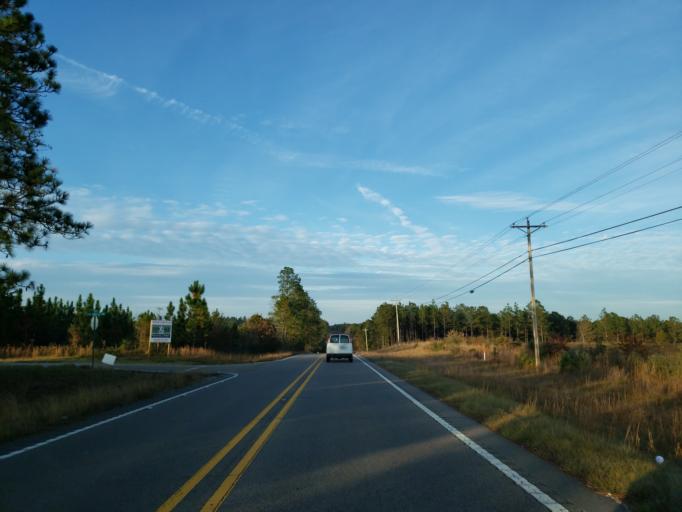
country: US
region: Mississippi
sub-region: Lamar County
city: West Hattiesburg
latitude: 31.2254
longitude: -89.3544
